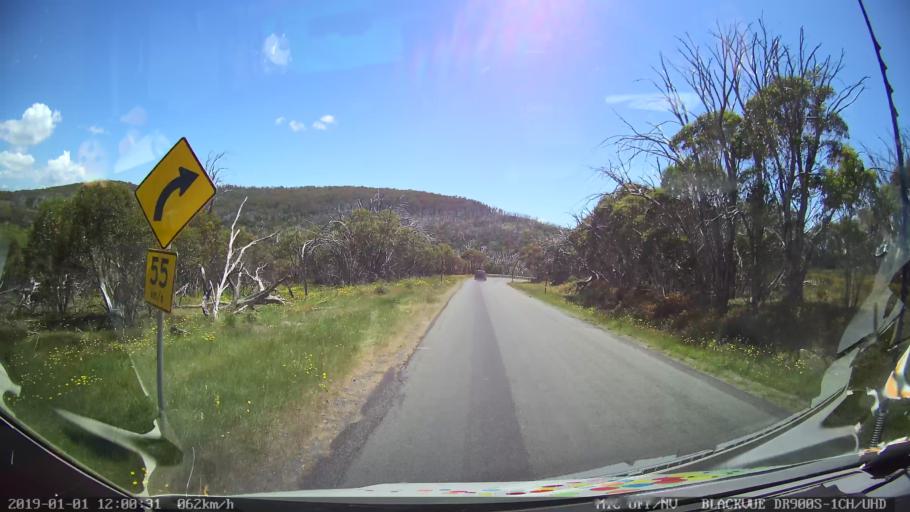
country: AU
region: New South Wales
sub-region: Snowy River
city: Jindabyne
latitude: -35.8840
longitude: 148.4597
